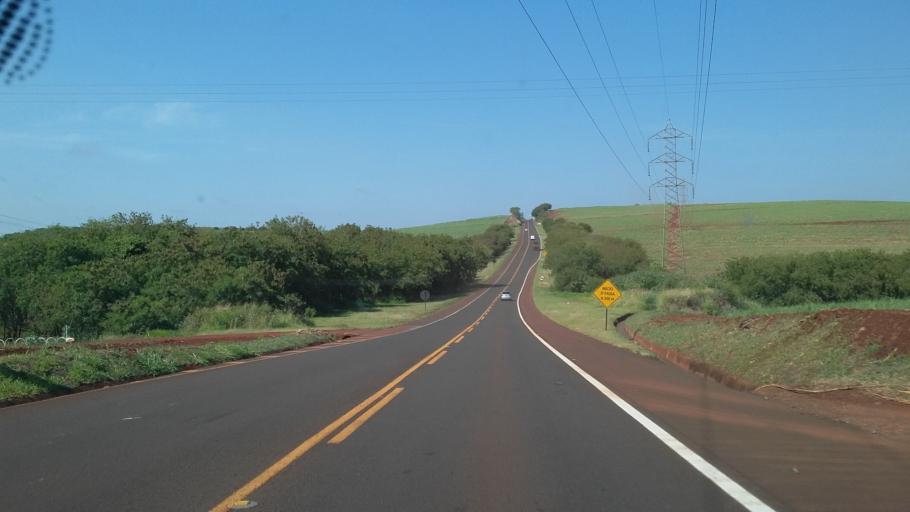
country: BR
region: Parana
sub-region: Bandeirantes
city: Bandeirantes
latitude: -23.1172
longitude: -50.3446
